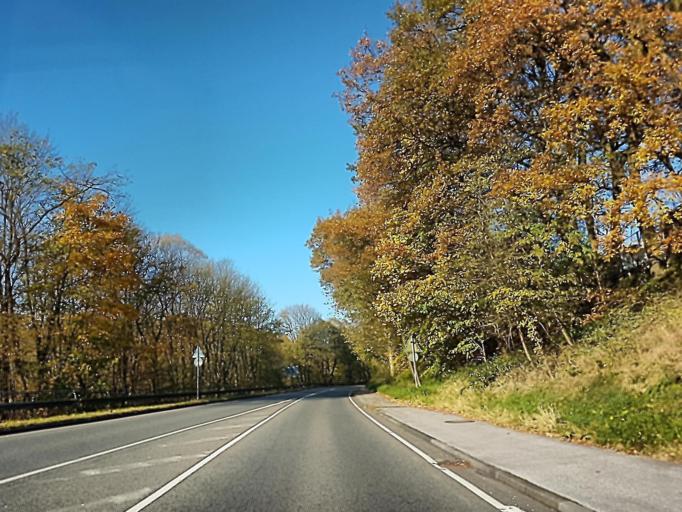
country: DE
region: North Rhine-Westphalia
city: Huckeswagen
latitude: 51.1874
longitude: 7.2832
